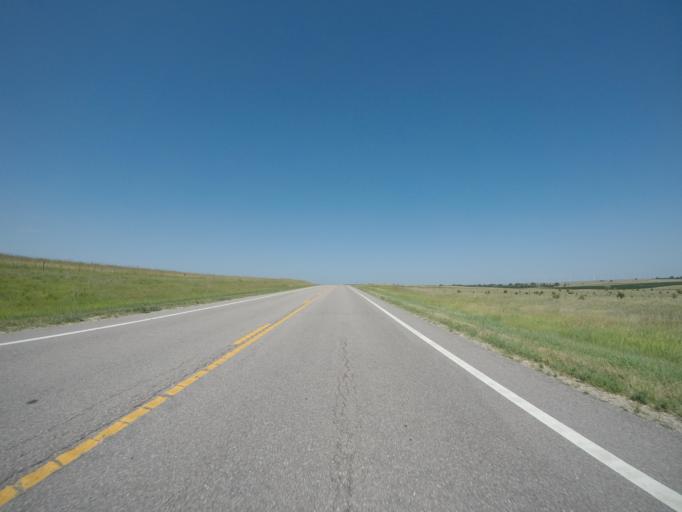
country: US
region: Kansas
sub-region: Cloud County
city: Concordia
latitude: 39.3645
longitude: -97.4662
